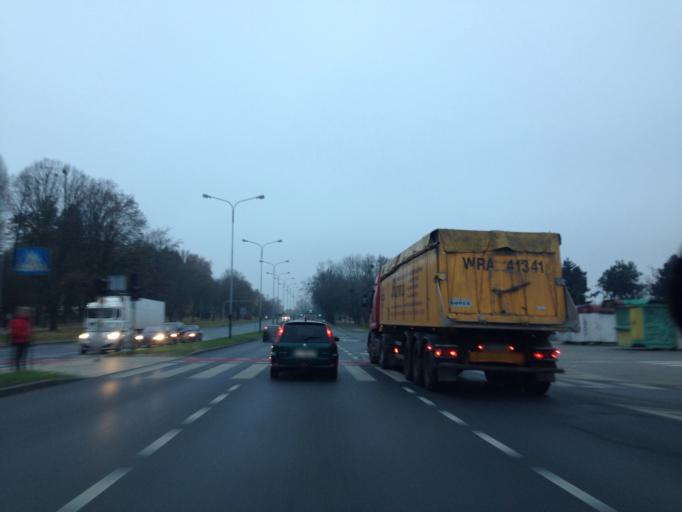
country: PL
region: Lodz Voivodeship
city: Lodz
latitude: 51.7911
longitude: 19.4873
